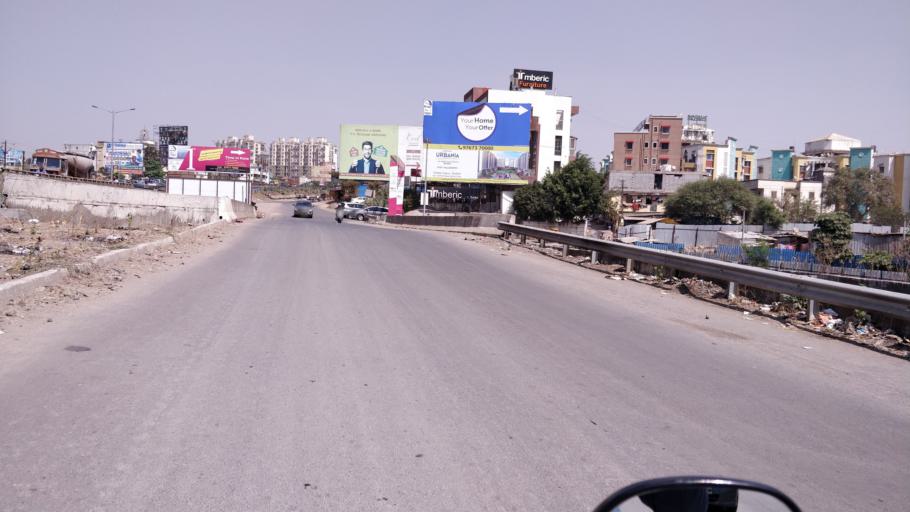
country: IN
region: Maharashtra
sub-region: Pune Division
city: Kharakvasla
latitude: 18.5130
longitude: 73.7704
